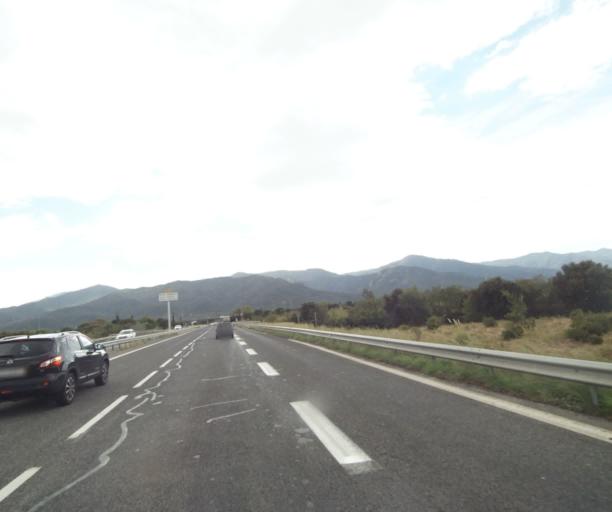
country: FR
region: Languedoc-Roussillon
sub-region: Departement des Pyrenees-Orientales
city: Argelers
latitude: 42.5538
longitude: 3.0060
